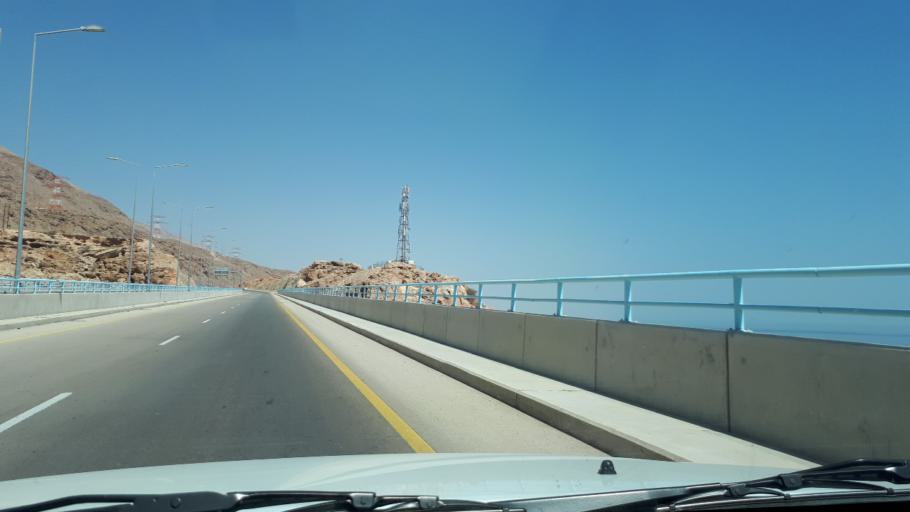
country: OM
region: Ash Sharqiyah
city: Sur
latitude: 22.8220
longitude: 59.2605
